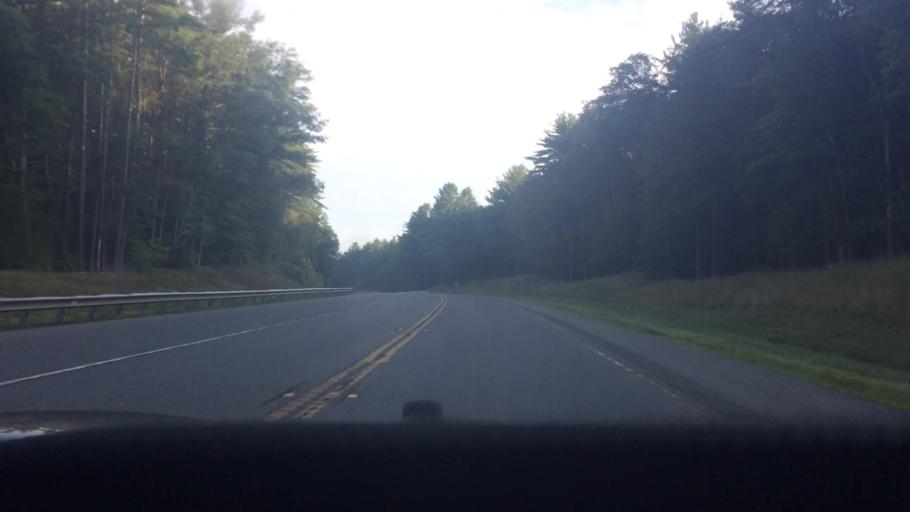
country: US
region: Massachusetts
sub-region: Franklin County
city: Orange
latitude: 42.5837
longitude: -72.3259
